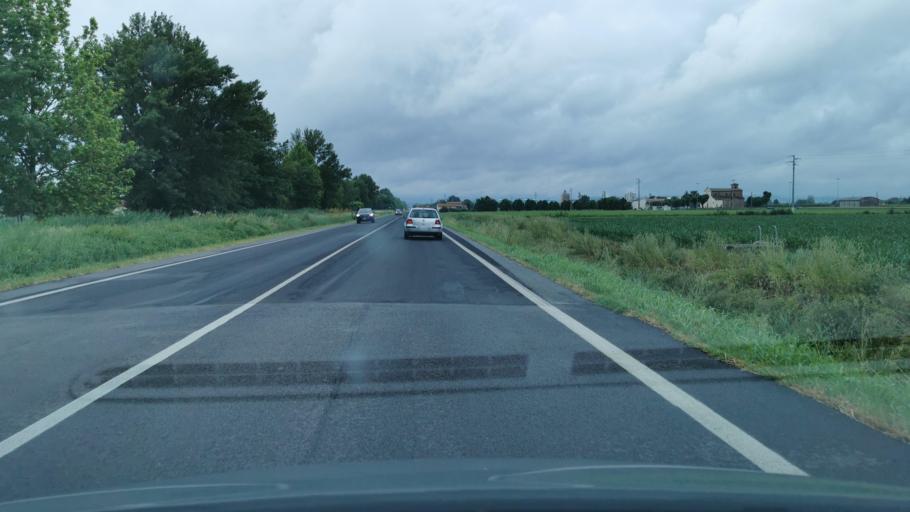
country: IT
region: Emilia-Romagna
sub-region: Provincia di Ravenna
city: Granarolo
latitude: 44.3397
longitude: 11.9191
